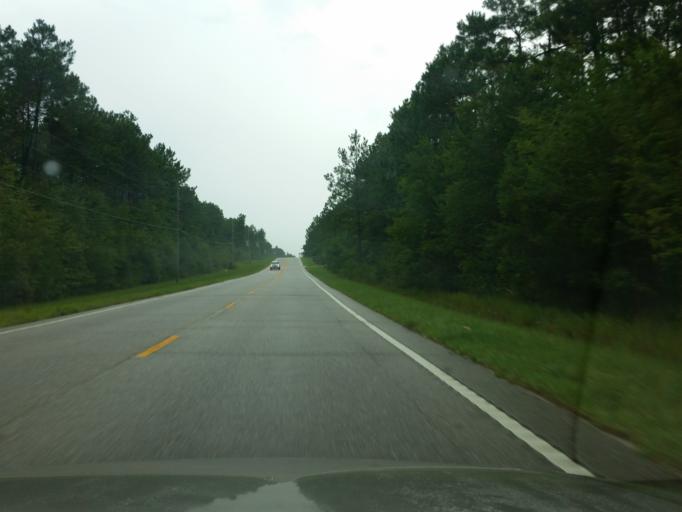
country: US
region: Alabama
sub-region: Baldwin County
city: Elberta
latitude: 30.5256
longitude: -87.5041
